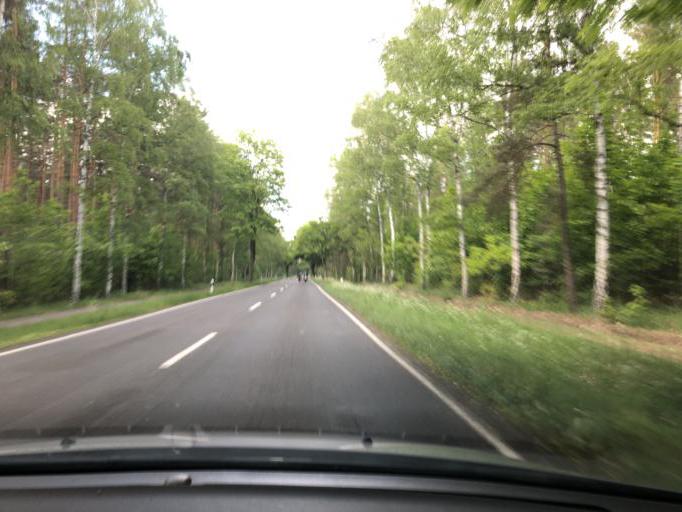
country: DE
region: Brandenburg
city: Grunheide
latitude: 52.3791
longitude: 13.8323
